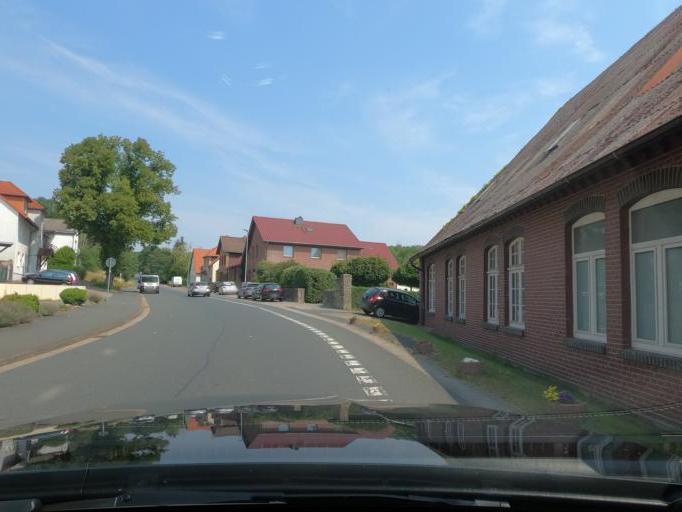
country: DE
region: Lower Saxony
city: Springe
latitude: 52.2193
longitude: 9.6235
